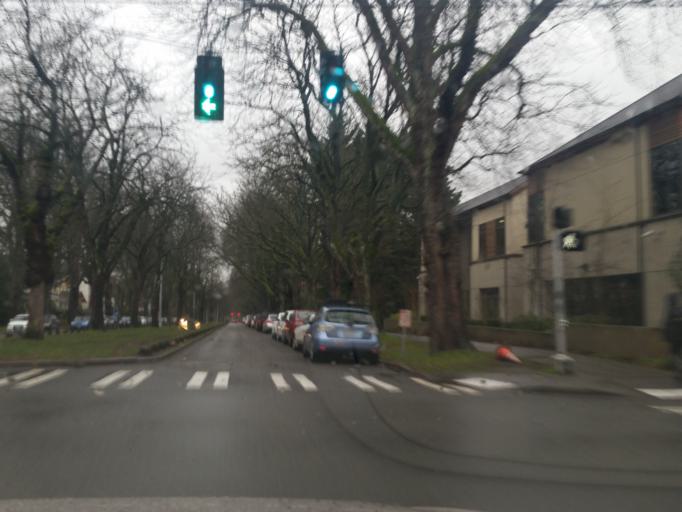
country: US
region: Washington
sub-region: King County
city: Seattle
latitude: 47.6650
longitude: -122.3097
